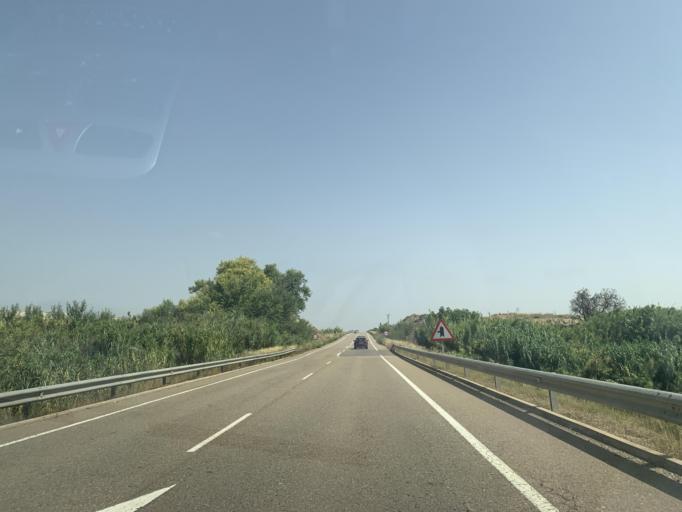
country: ES
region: Aragon
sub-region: Provincia de Zaragoza
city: Fuentes de Ebro
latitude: 41.4592
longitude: -0.7251
